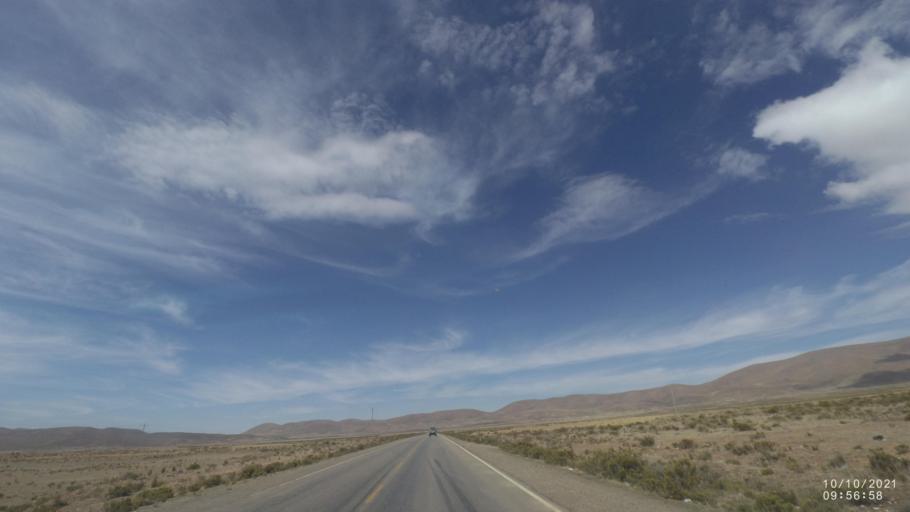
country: BO
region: La Paz
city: Colquiri
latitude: -17.3296
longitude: -67.3801
